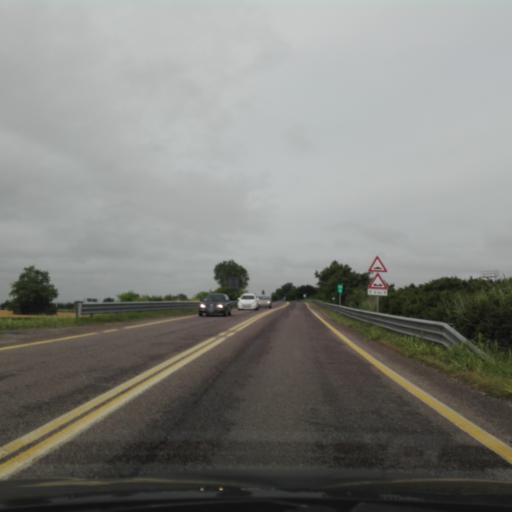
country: IT
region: Veneto
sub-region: Provincia di Rovigo
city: Grignano Polesine
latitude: 45.0794
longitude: 11.7433
